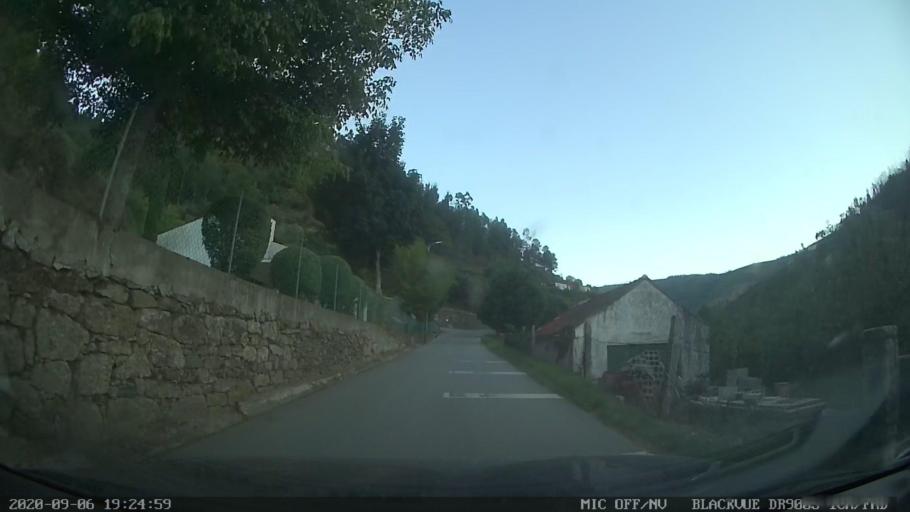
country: PT
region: Vila Real
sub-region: Mesao Frio
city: Mesao Frio
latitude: 41.1893
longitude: -7.9216
